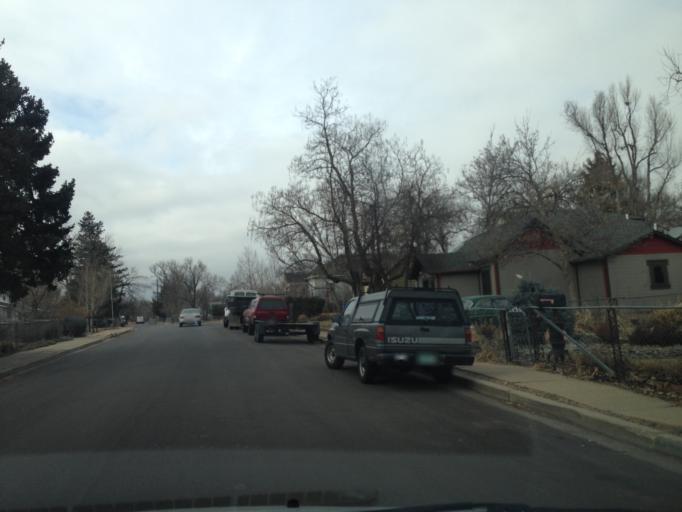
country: US
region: Colorado
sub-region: Boulder County
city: Lafayette
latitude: 39.9944
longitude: -105.0866
